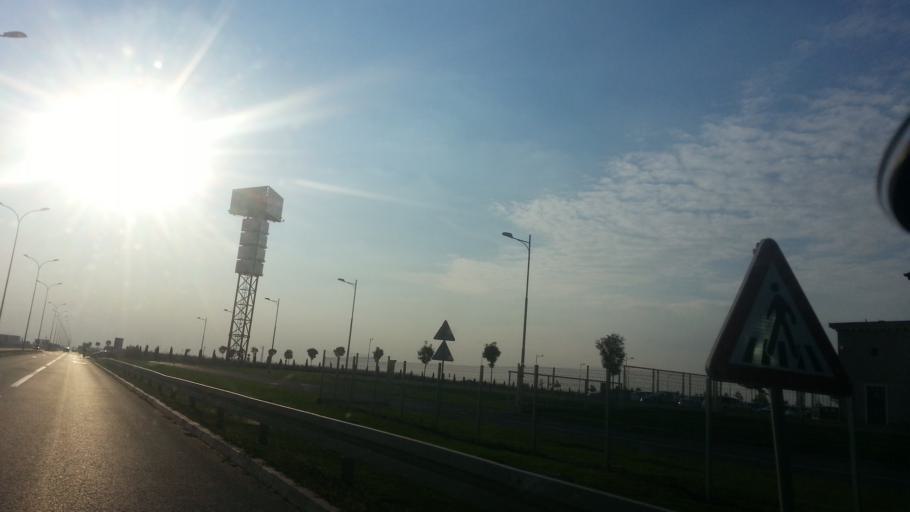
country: RS
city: Novi Karlovci
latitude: 45.0677
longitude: 20.1379
